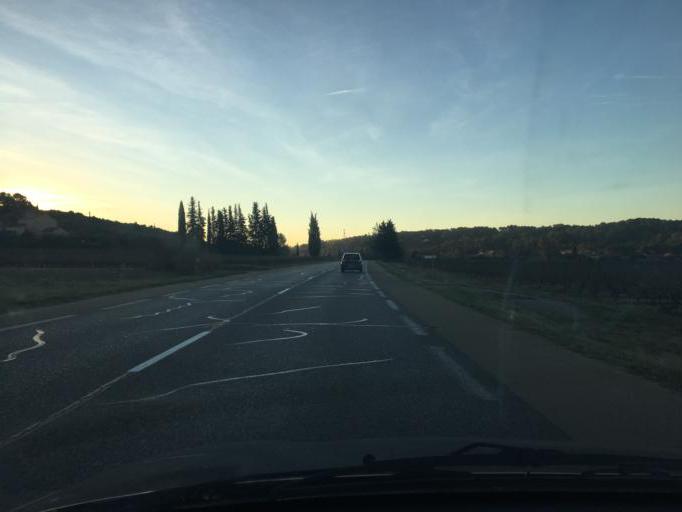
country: FR
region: Provence-Alpes-Cote d'Azur
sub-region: Departement du Var
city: Lorgues
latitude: 43.4818
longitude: 6.3704
